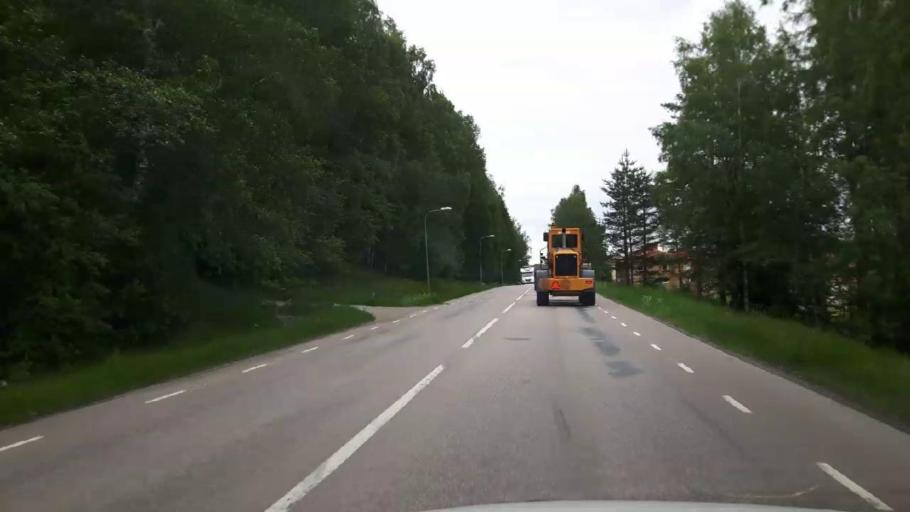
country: SE
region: Vaestmanland
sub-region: Kopings Kommun
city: Kolsva
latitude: 59.6070
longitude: 15.8311
